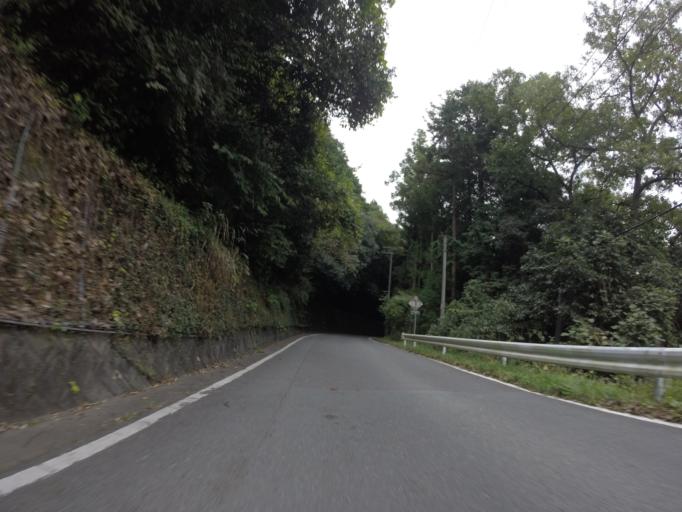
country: JP
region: Shizuoka
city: Mori
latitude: 34.8567
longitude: 138.0136
